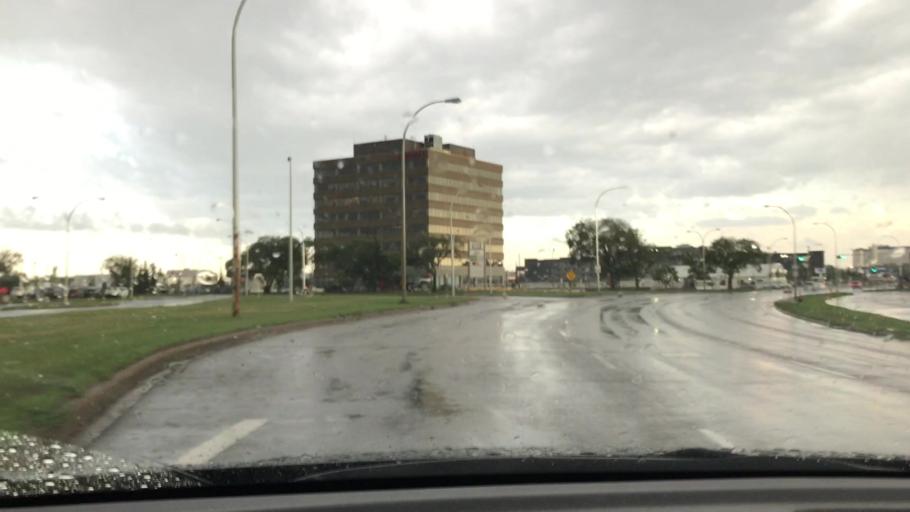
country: CA
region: Alberta
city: Edmonton
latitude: 53.4917
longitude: -113.4953
